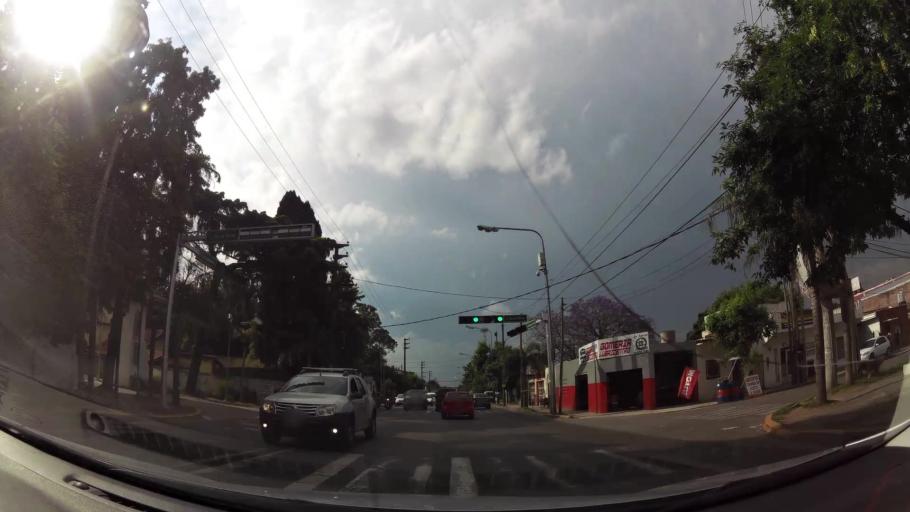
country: AR
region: Buenos Aires
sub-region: Partido de Tigre
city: Tigre
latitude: -34.4799
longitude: -58.6231
